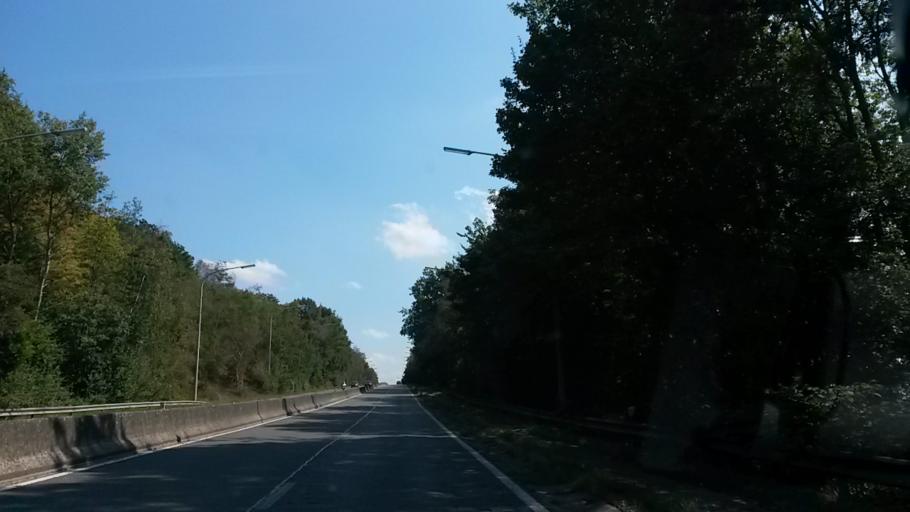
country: BE
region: Wallonia
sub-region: Province du Hainaut
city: Aiseau
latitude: 50.4569
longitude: 4.6284
